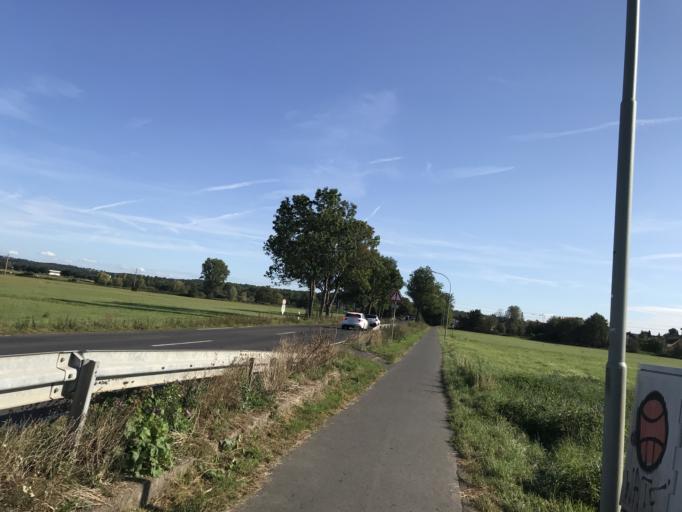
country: DE
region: Hesse
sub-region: Regierungsbezirk Darmstadt
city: Altenstadt
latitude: 50.2806
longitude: 8.9457
